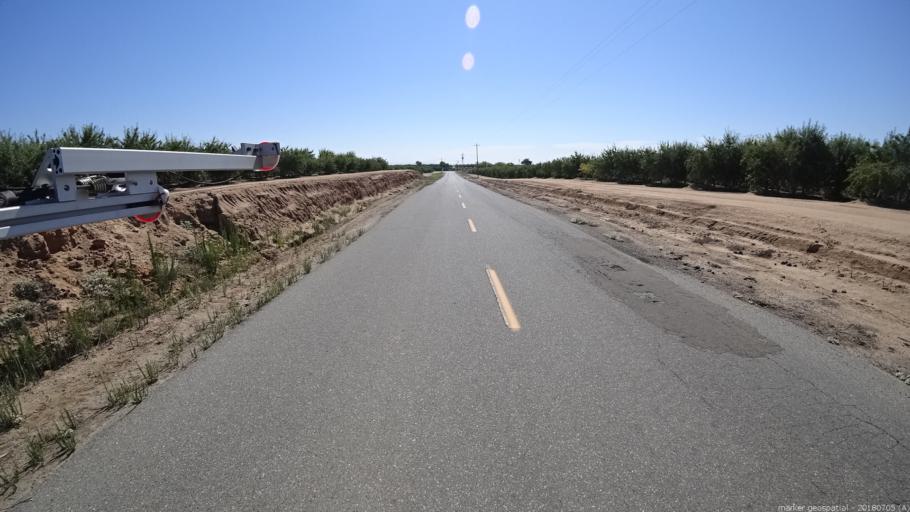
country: US
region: California
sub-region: Madera County
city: Madera Acres
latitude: 37.0980
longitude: -120.0787
